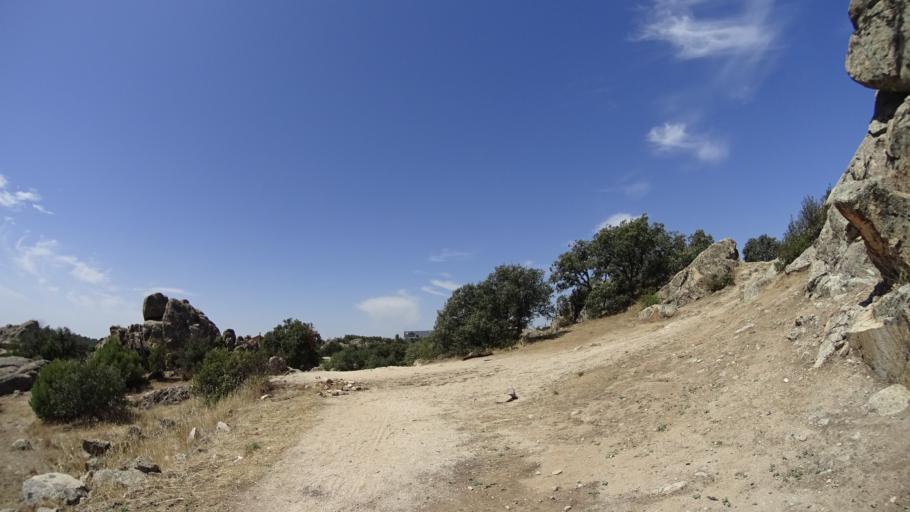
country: ES
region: Madrid
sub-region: Provincia de Madrid
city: Torrelodones
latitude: 40.5737
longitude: -3.9324
